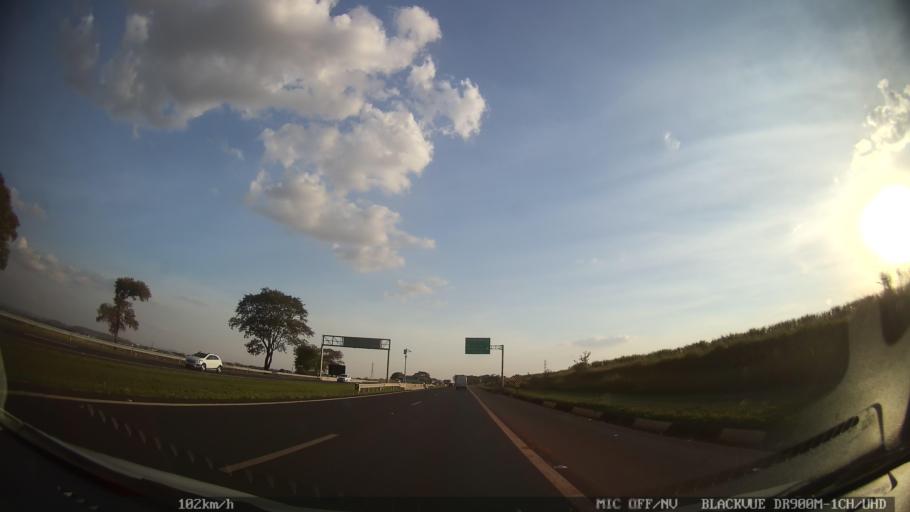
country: BR
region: Sao Paulo
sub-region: Ribeirao Preto
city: Ribeirao Preto
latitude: -21.1076
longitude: -47.7705
